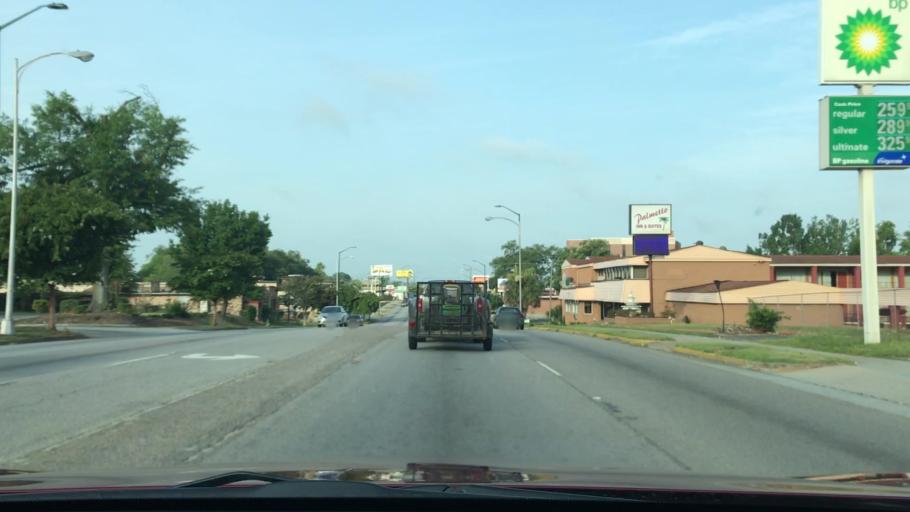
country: US
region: South Carolina
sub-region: Orangeburg County
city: Orangeburg
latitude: 33.4899
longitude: -80.8579
